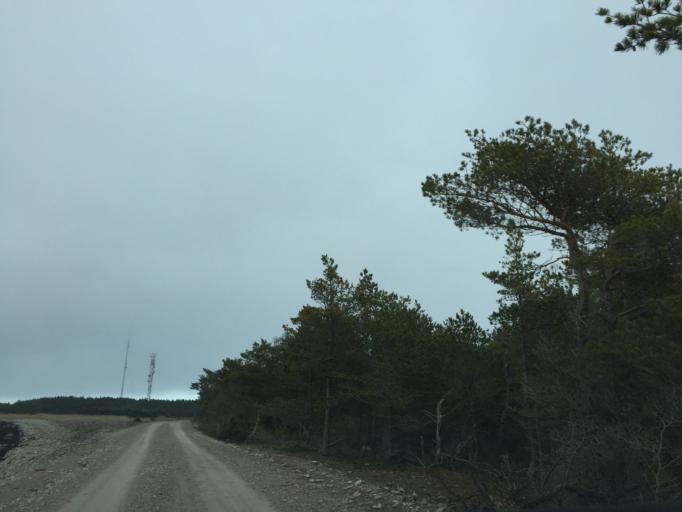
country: EE
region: Saare
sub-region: Kuressaare linn
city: Kuressaare
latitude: 58.5096
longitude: 21.9145
